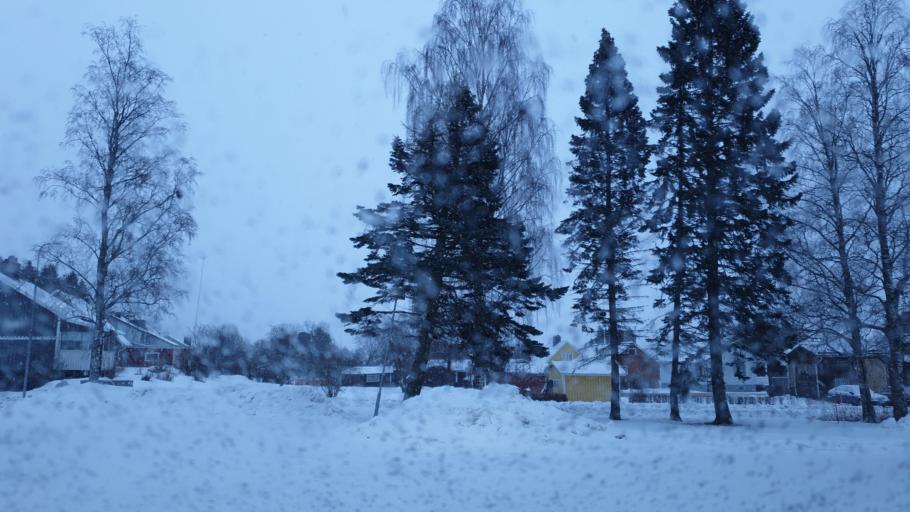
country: SE
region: Vaesternorrland
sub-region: OErnskoeldsviks Kommun
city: Ornskoldsvik
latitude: 63.2920
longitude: 18.6179
